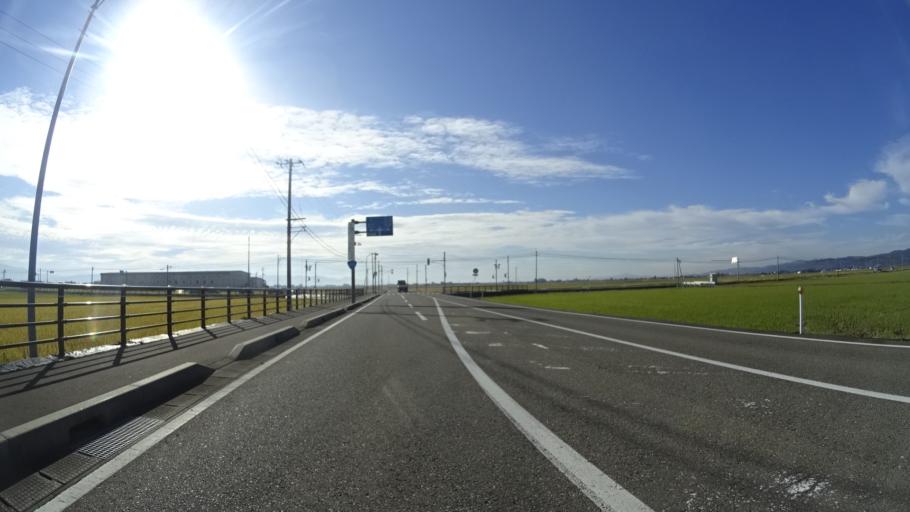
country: JP
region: Niigata
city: Mitsuke
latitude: 37.5561
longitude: 138.8492
